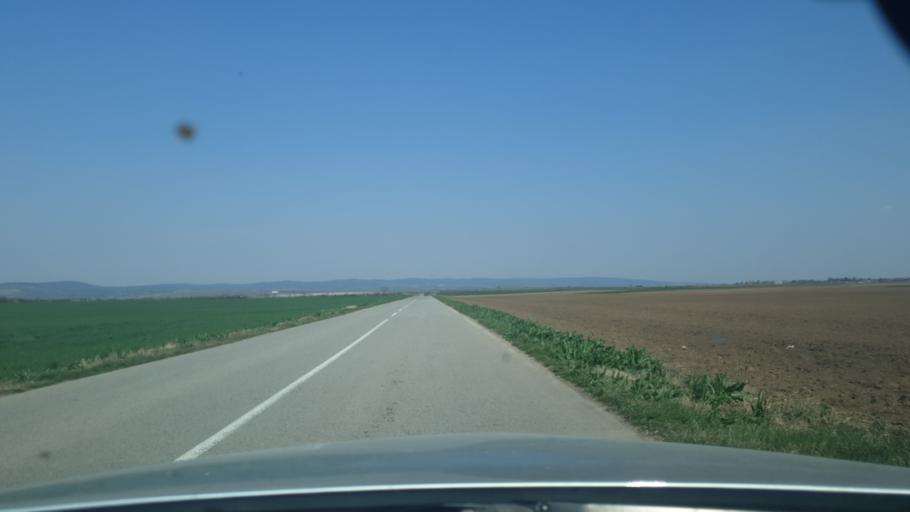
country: RS
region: Autonomna Pokrajina Vojvodina
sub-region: Sremski Okrug
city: Ruma
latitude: 45.0442
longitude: 19.7609
